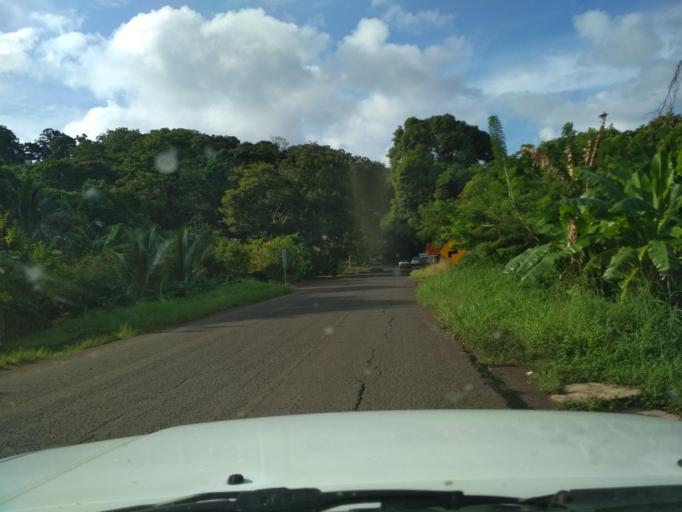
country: MX
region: Veracruz
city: Catemaco
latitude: 18.3878
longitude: -95.1229
